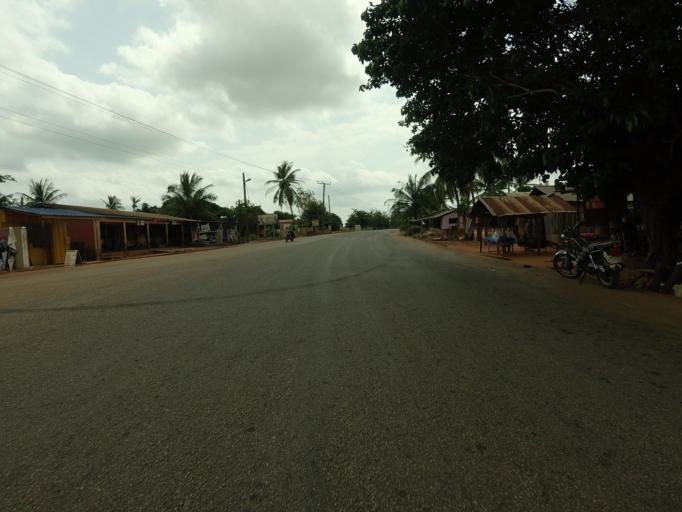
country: TG
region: Maritime
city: Lome
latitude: 6.1741
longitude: 1.0723
